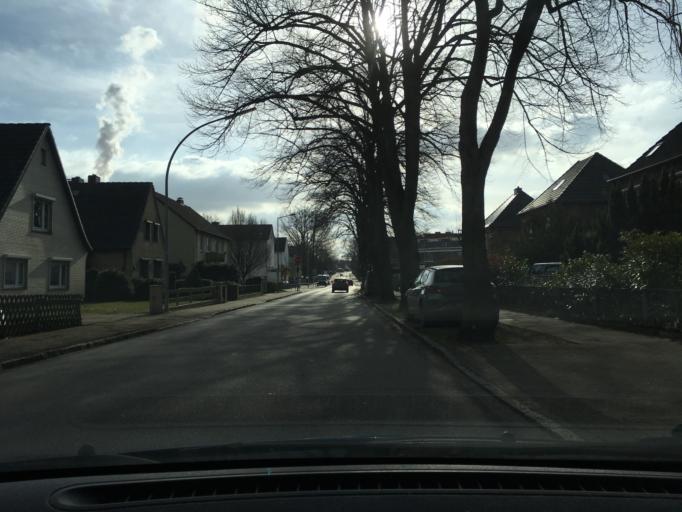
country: DE
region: Schleswig-Holstein
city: Wedel
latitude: 53.5780
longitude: 9.7223
